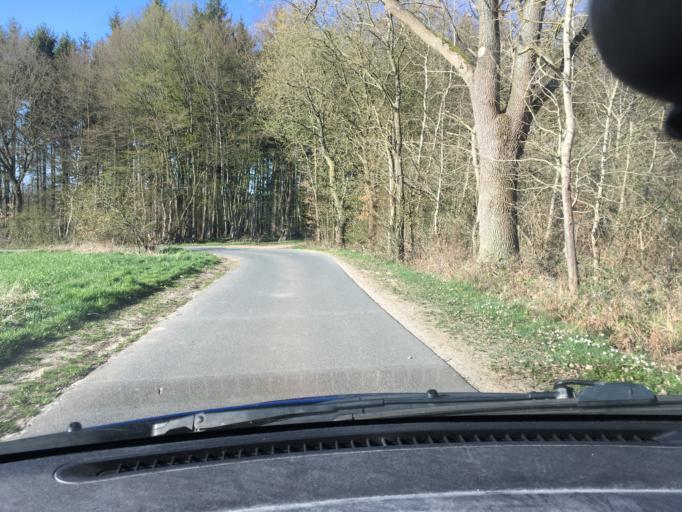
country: DE
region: Lower Saxony
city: Rehlingen
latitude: 53.1194
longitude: 10.2346
